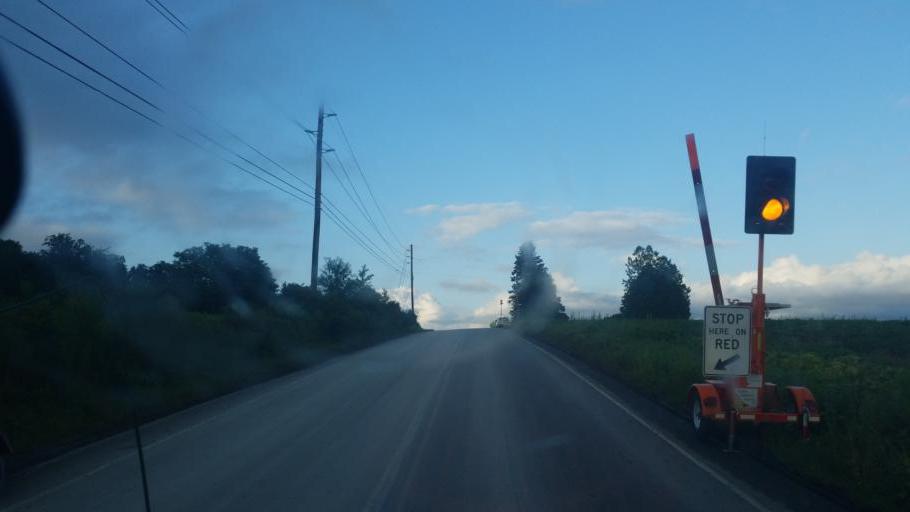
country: US
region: Pennsylvania
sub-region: Potter County
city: Galeton
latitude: 41.8533
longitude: -77.7697
